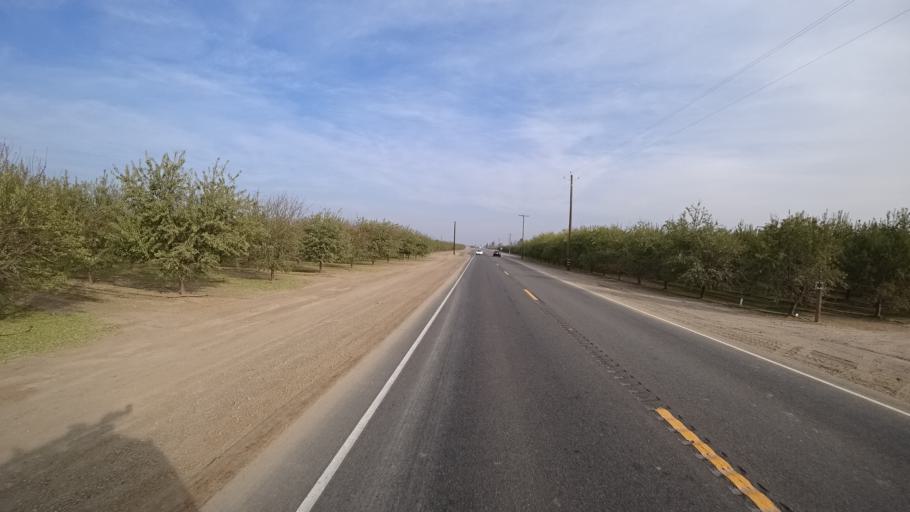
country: US
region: California
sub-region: Kern County
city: Rosedale
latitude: 35.2672
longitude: -119.1327
